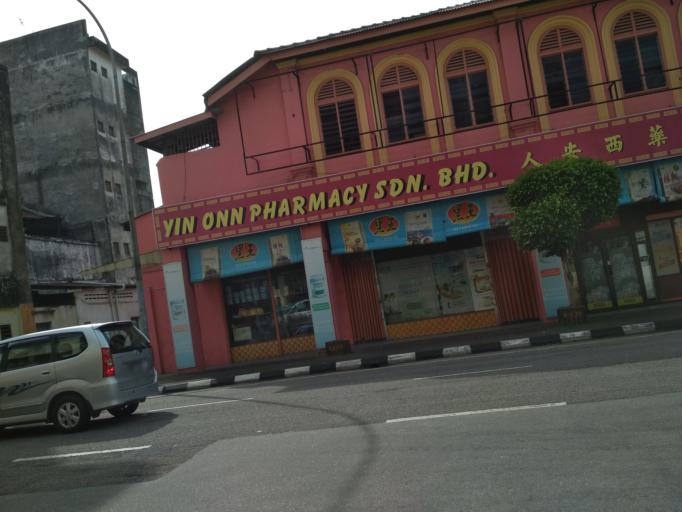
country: MY
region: Perak
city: Ipoh
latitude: 4.5945
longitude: 101.0826
